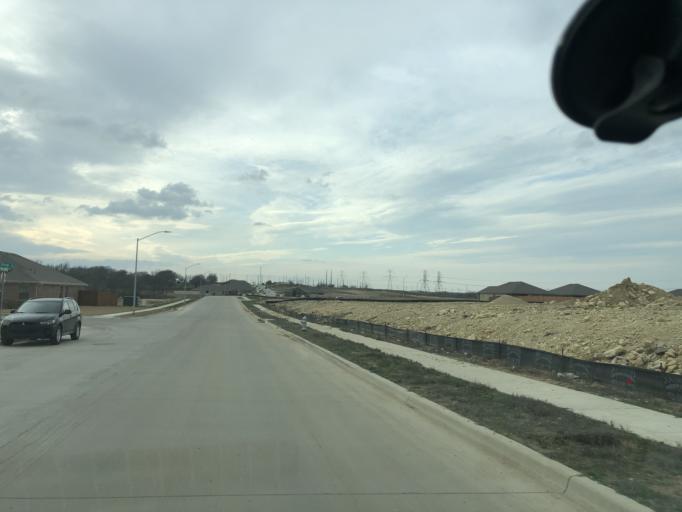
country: US
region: Texas
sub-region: Tarrant County
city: Saginaw
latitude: 32.9031
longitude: -97.3681
